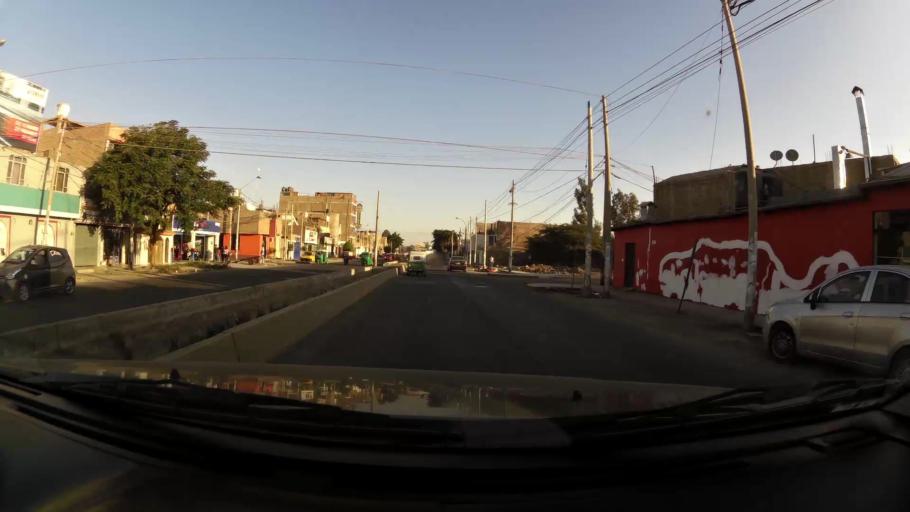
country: PE
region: Ica
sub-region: Provincia de Ica
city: Ica
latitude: -14.0680
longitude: -75.7354
